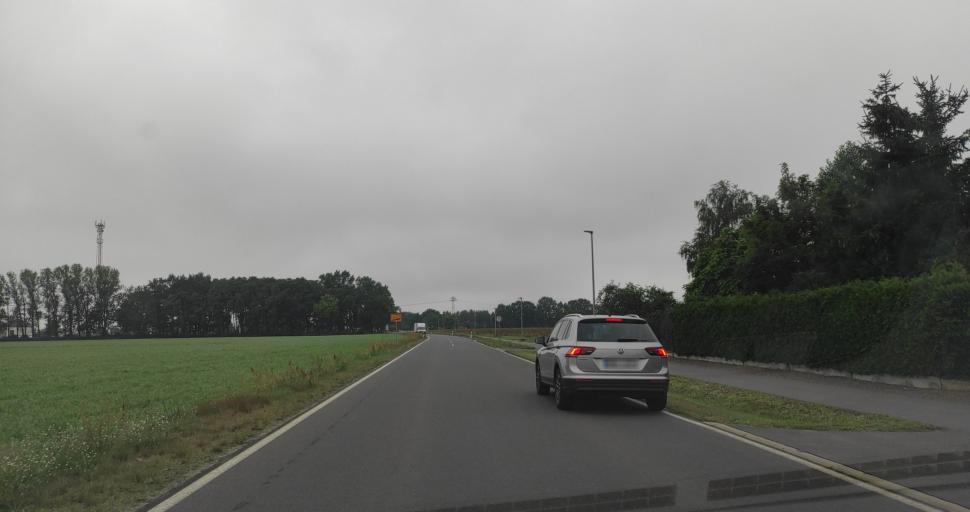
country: DE
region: Brandenburg
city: Forst
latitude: 51.7180
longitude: 14.6338
